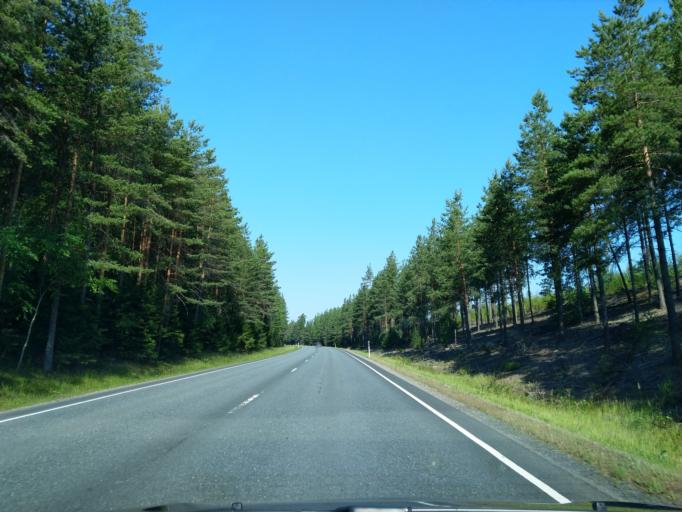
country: FI
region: Haeme
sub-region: Forssa
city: Humppila
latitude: 60.9715
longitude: 23.2719
